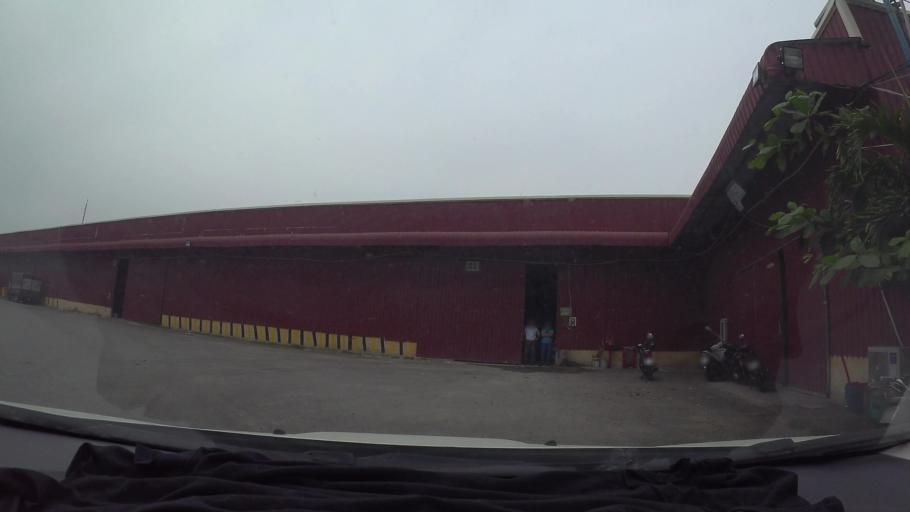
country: VN
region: Da Nang
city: Cam Le
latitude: 16.0281
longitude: 108.2080
